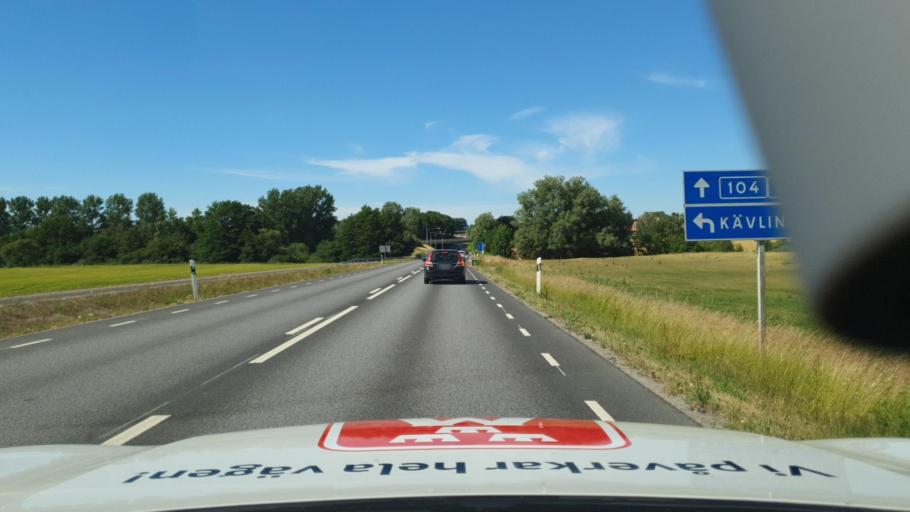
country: SE
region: Skane
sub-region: Kavlinge Kommun
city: Kaevlinge
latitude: 55.7898
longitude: 13.1315
